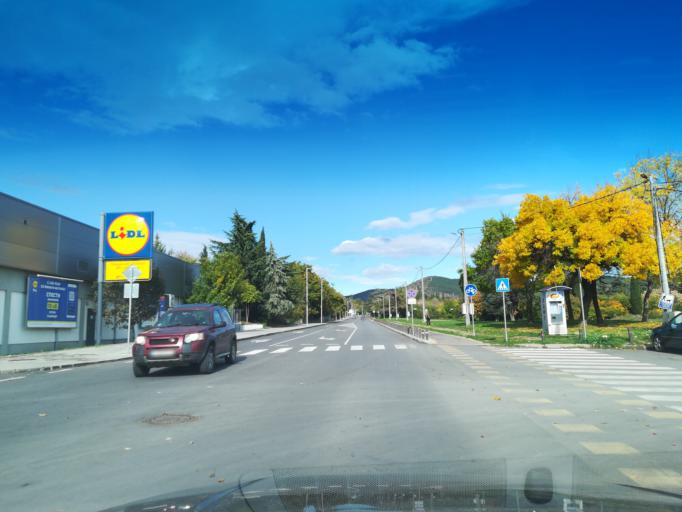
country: BG
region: Stara Zagora
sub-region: Obshtina Stara Zagora
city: Stara Zagora
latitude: 42.4387
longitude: 25.6357
